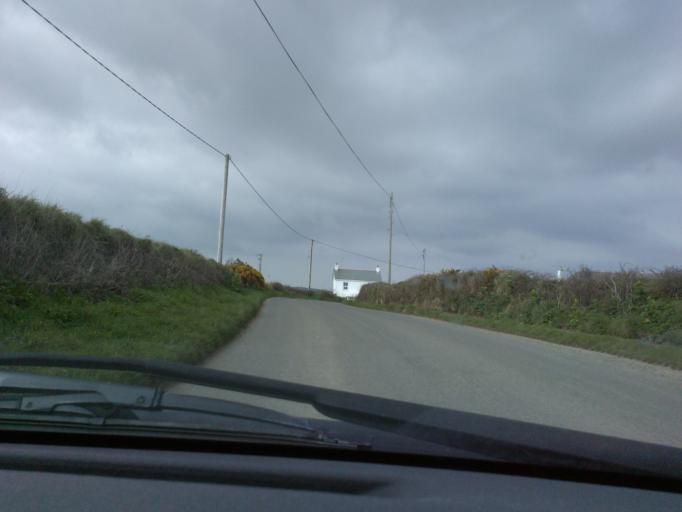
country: GB
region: England
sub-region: Cornwall
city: St. Buryan
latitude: 50.0535
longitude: -5.6590
